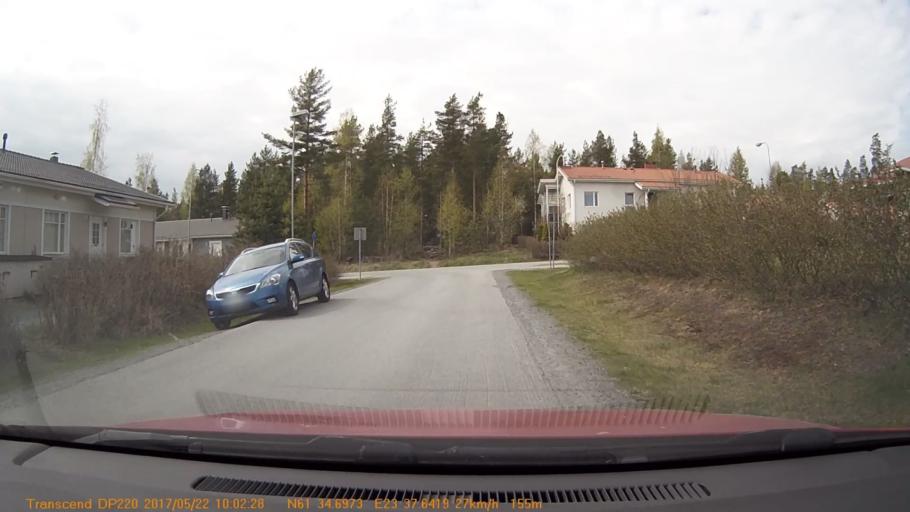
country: FI
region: Pirkanmaa
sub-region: Tampere
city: Yloejaervi
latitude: 61.5784
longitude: 23.6270
